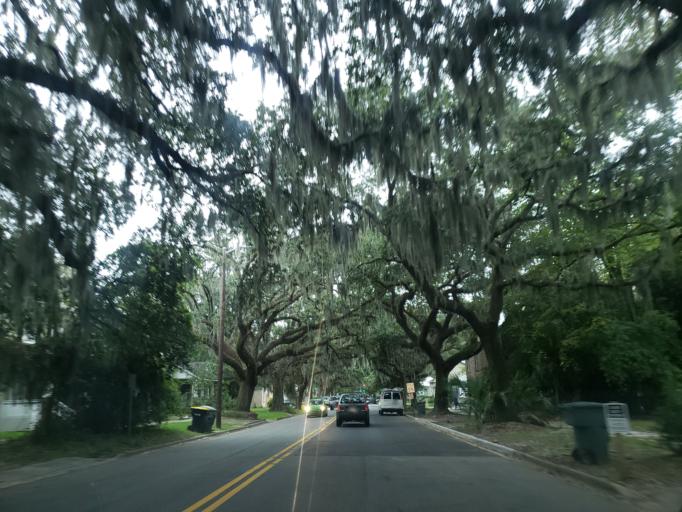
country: US
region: Georgia
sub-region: Chatham County
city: Savannah
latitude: 32.0544
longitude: -81.0896
